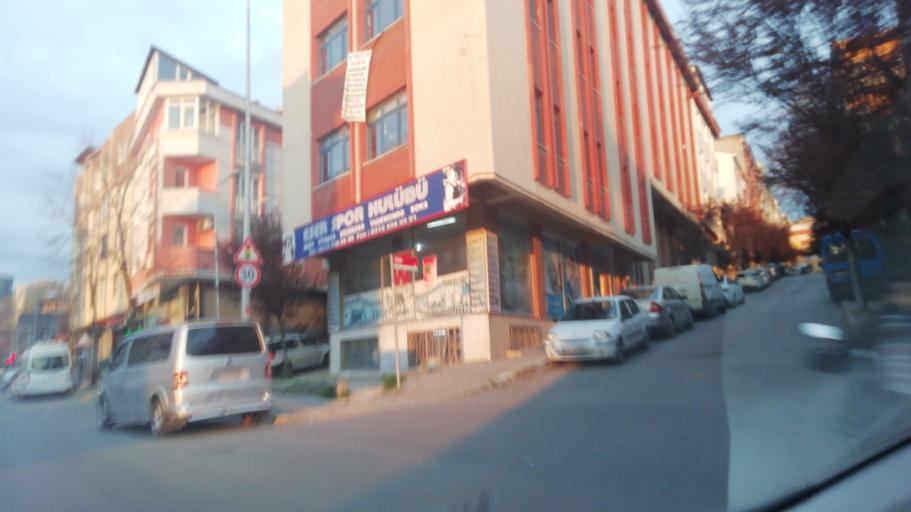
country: TR
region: Istanbul
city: Mahmutbey
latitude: 41.0374
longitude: 28.8239
